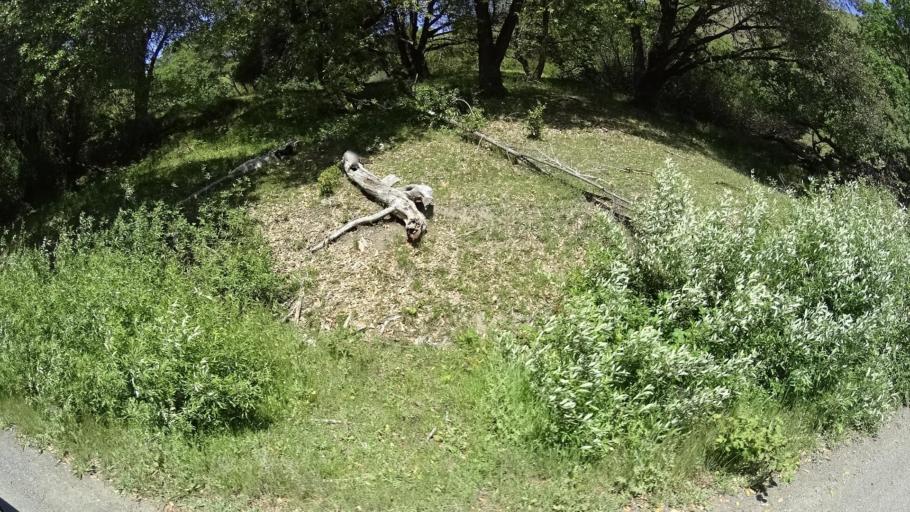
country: US
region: California
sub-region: Humboldt County
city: Redway
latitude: 40.1938
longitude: -123.5666
